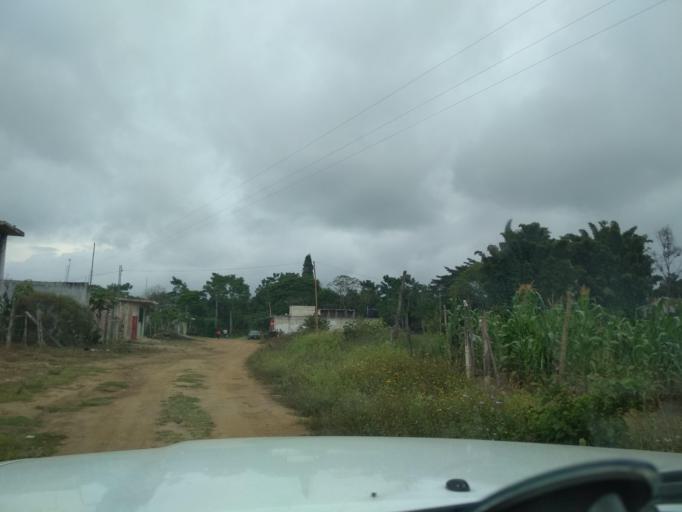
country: MX
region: Veracruz
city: El Castillo
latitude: 19.5432
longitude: -96.8486
